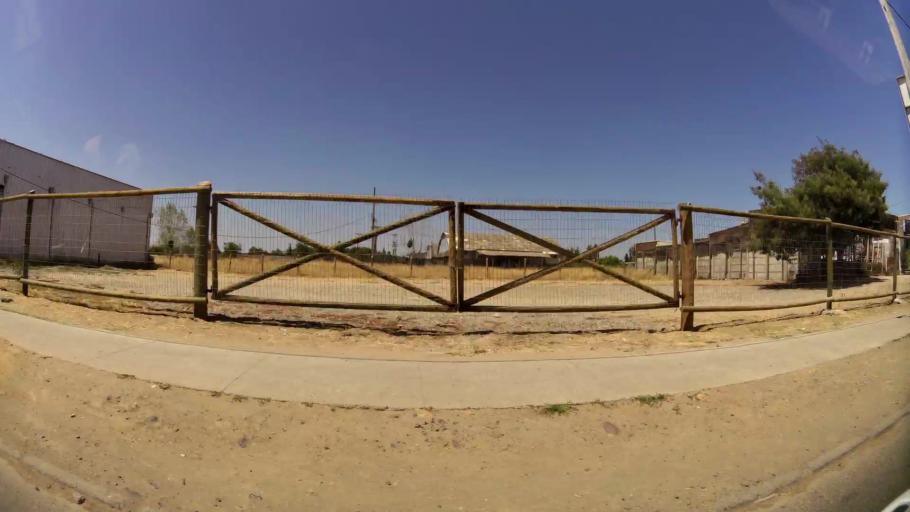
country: CL
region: Maule
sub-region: Provincia de Talca
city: Talca
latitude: -35.4330
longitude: -71.6285
